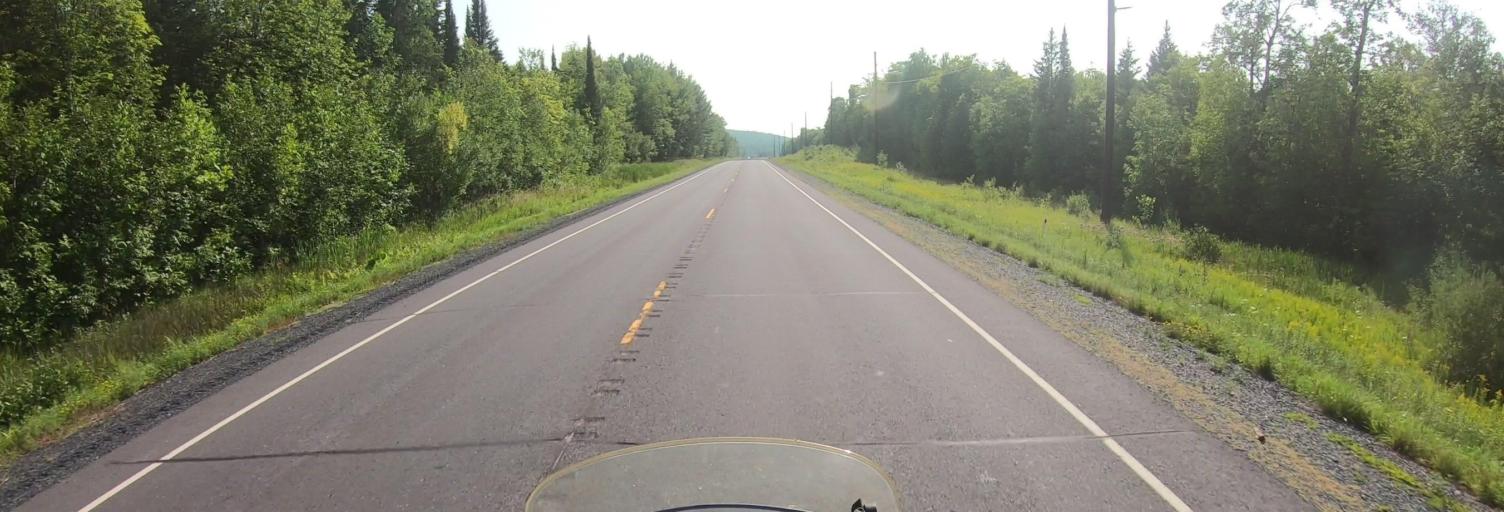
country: US
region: Wisconsin
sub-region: Iron County
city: Hurley
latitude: 46.3860
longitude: -90.3601
